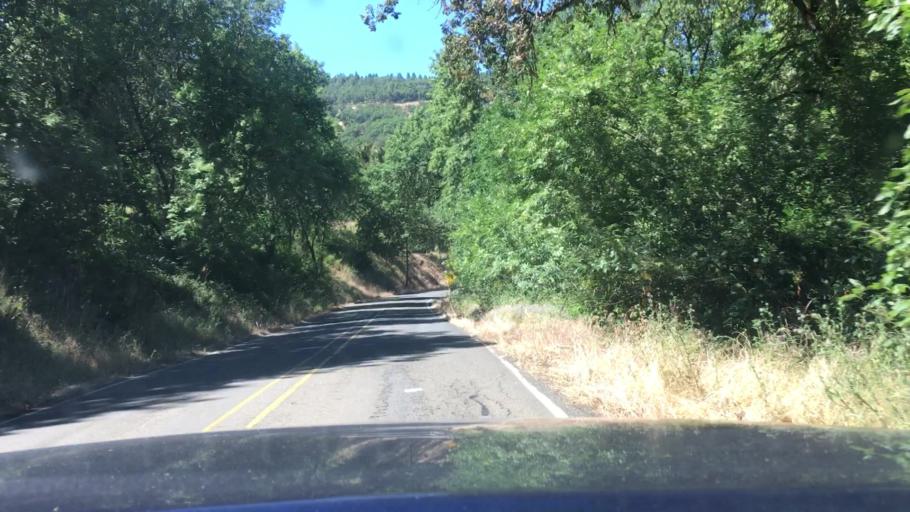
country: US
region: Oregon
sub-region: Douglas County
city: Winston
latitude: 43.1416
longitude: -123.4150
